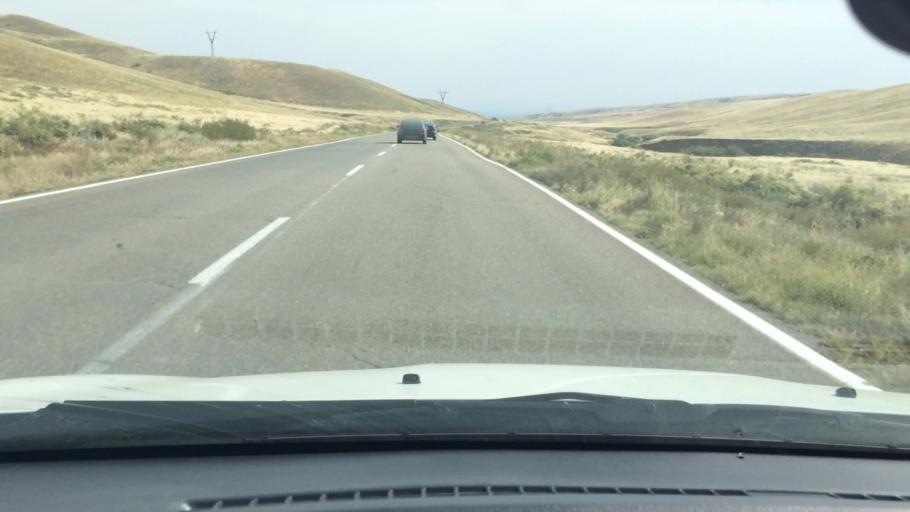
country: GE
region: Kvemo Kartli
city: Rust'avi
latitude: 41.5161
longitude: 44.9440
